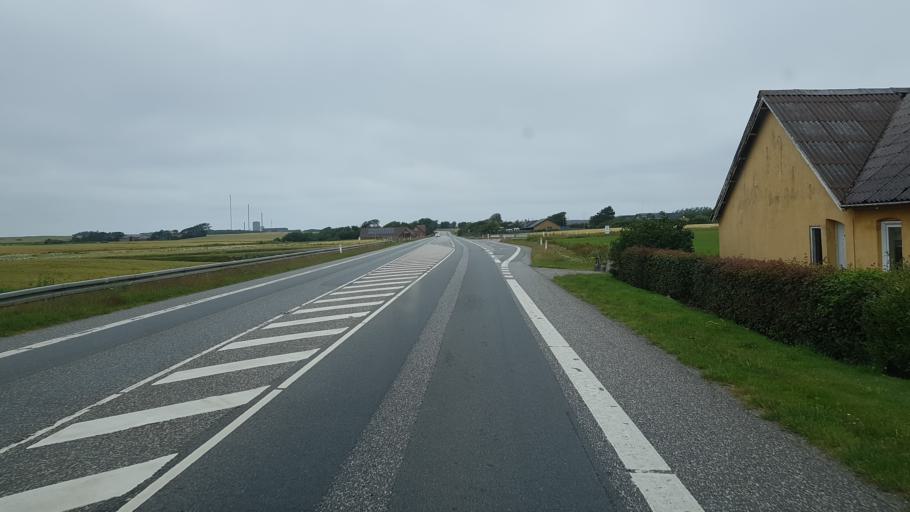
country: DK
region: Central Jutland
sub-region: Lemvig Kommune
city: Lemvig
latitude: 56.5200
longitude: 8.3068
